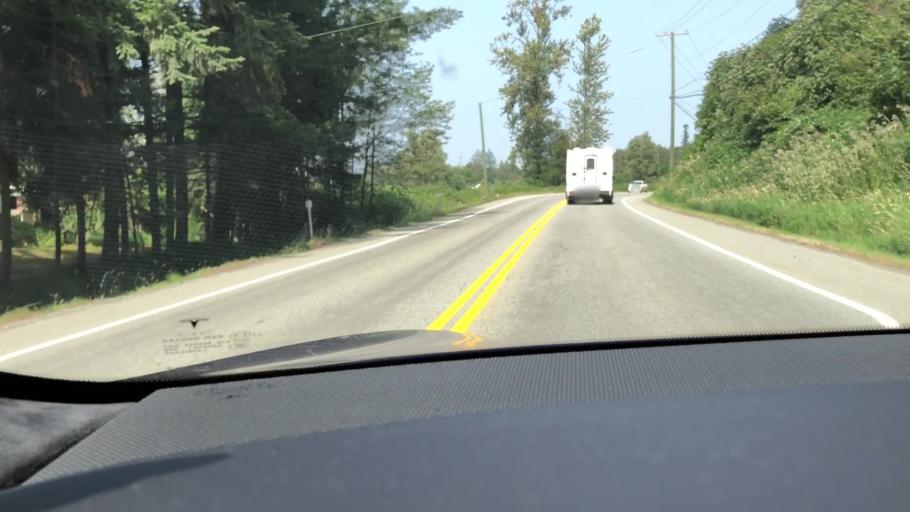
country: CA
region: British Columbia
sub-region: Fraser Valley Regional District
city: Chilliwack
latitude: 49.0855
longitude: -122.0269
